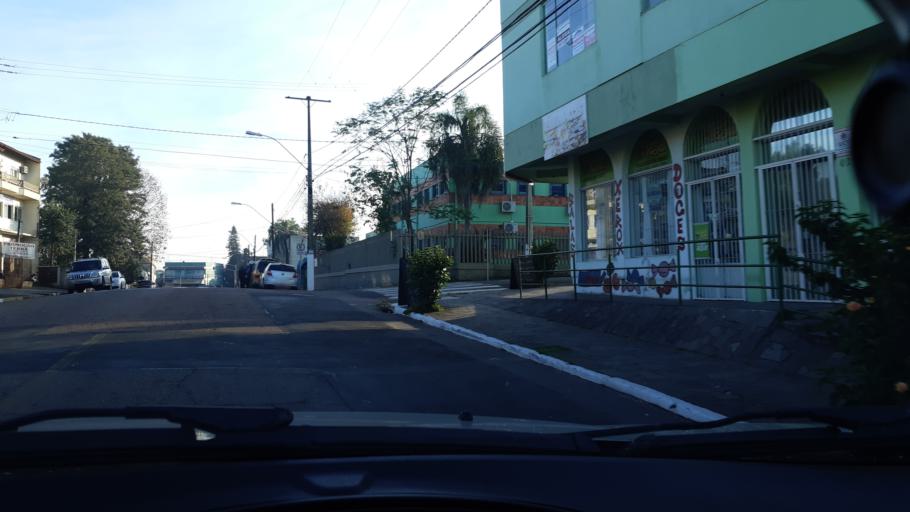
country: BR
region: Rio Grande do Sul
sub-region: Sapucaia Do Sul
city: Sapucaia
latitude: -29.8458
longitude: -51.1526
